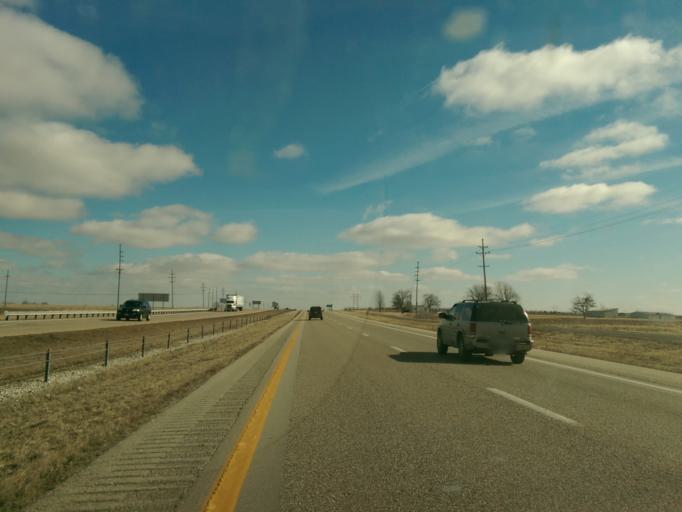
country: US
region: Missouri
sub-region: Montgomery County
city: Montgomery City
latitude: 38.8951
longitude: -91.4405
